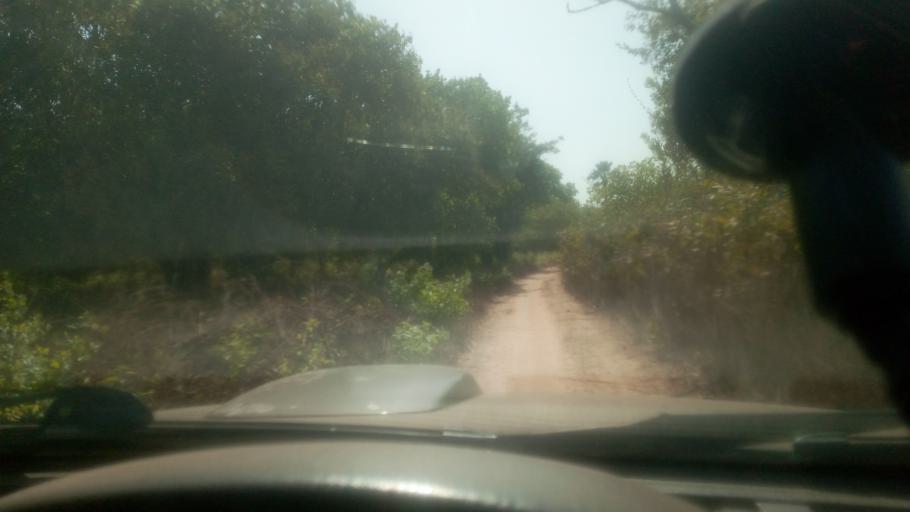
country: GW
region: Oio
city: Farim
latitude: 12.4537
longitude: -15.4147
